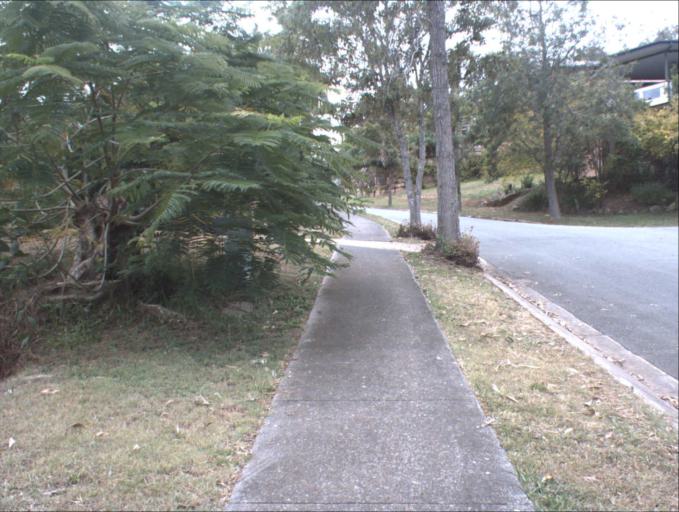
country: AU
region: Queensland
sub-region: Logan
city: Slacks Creek
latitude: -27.6760
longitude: 153.1692
